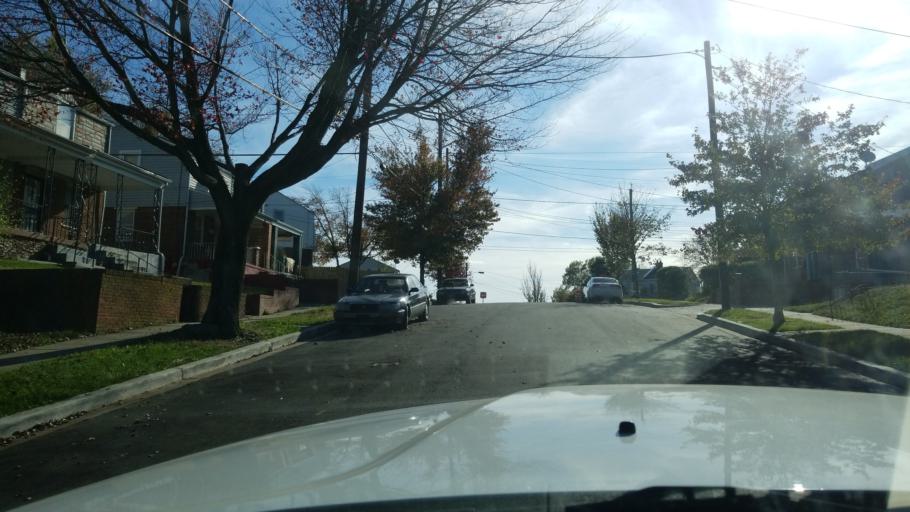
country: US
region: Maryland
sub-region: Prince George's County
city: Fairmount Heights
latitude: 38.9025
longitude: -76.9254
